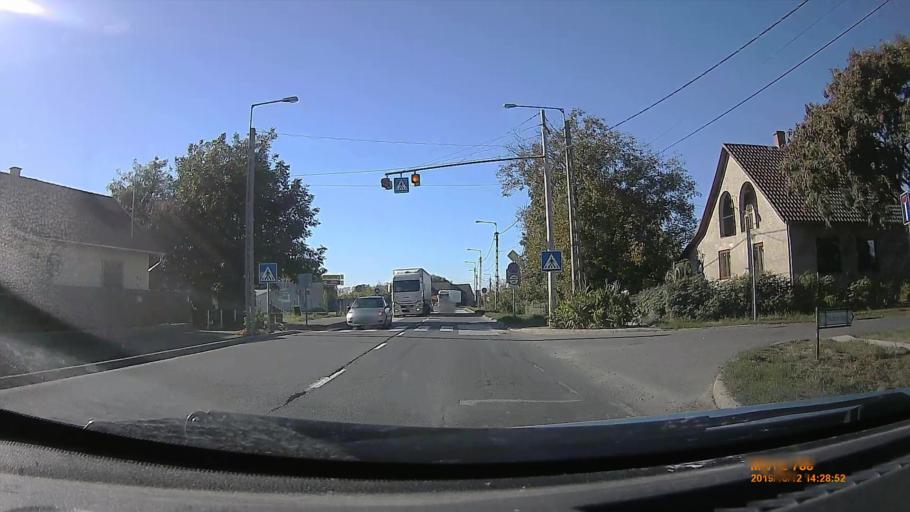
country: HU
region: Hajdu-Bihar
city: Berettyoujfalu
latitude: 47.1683
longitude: 21.6198
